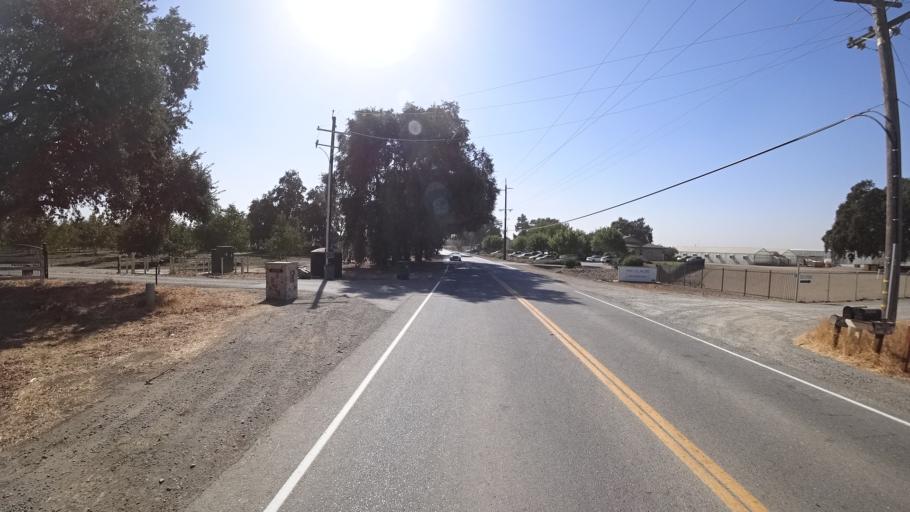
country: US
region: California
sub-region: Yolo County
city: Davis
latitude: 38.5240
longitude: -121.6951
